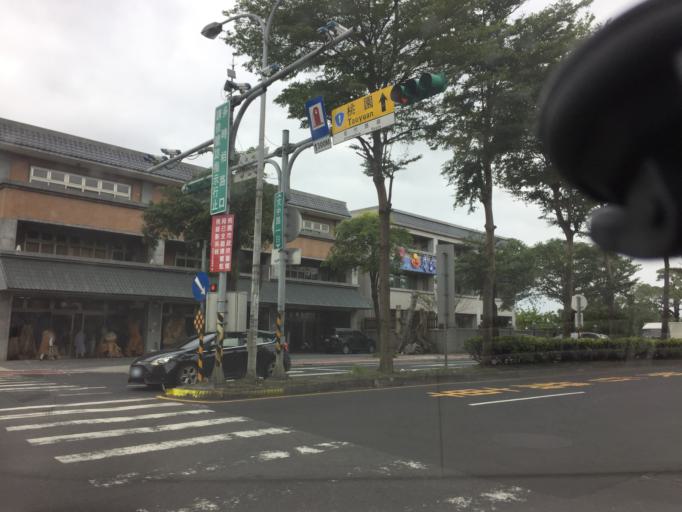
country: TW
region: Taiwan
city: Taoyuan City
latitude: 24.9913
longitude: 121.2674
